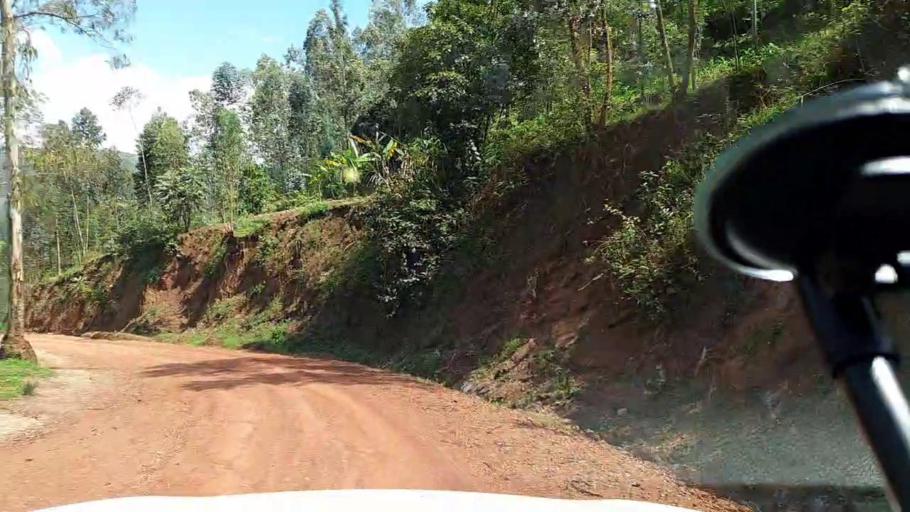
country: RW
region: Kigali
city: Kigali
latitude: -1.7981
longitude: 29.8868
